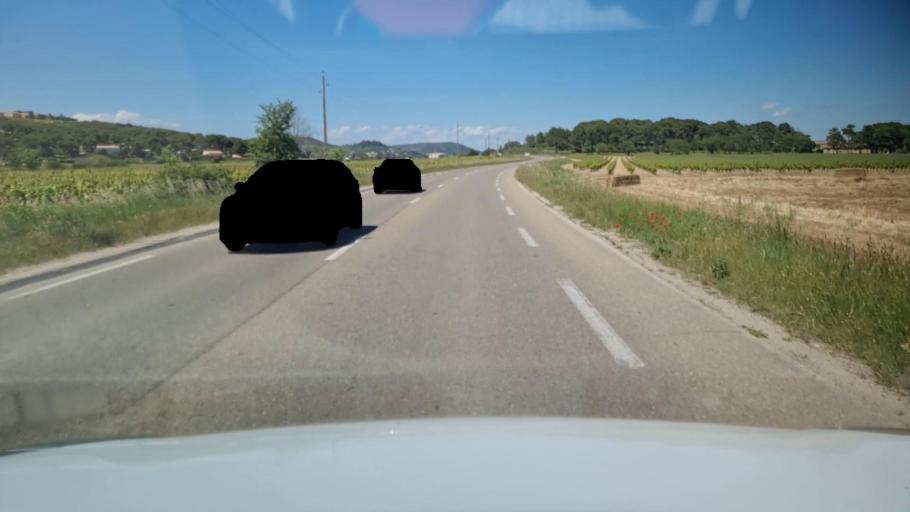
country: FR
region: Languedoc-Roussillon
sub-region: Departement du Gard
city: Mus
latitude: 43.7556
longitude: 4.2049
